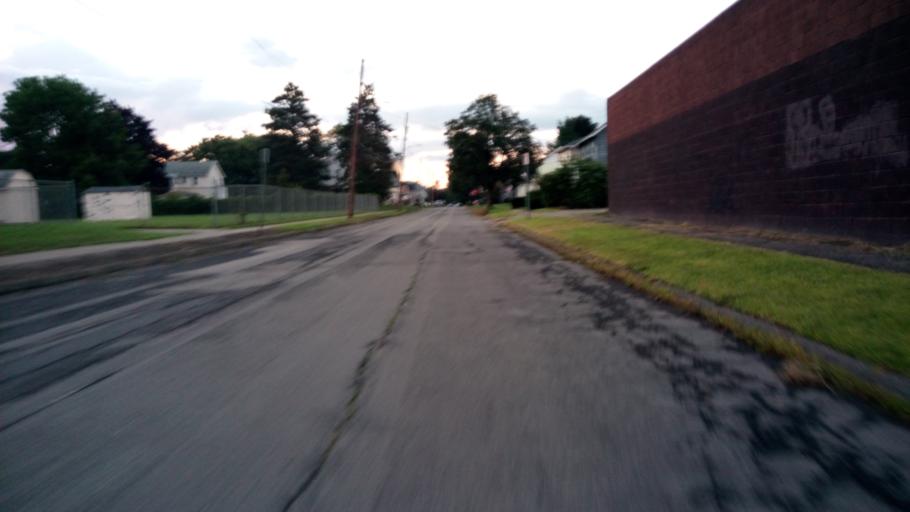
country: US
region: New York
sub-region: Chemung County
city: Elmira
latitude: 42.0977
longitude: -76.8206
